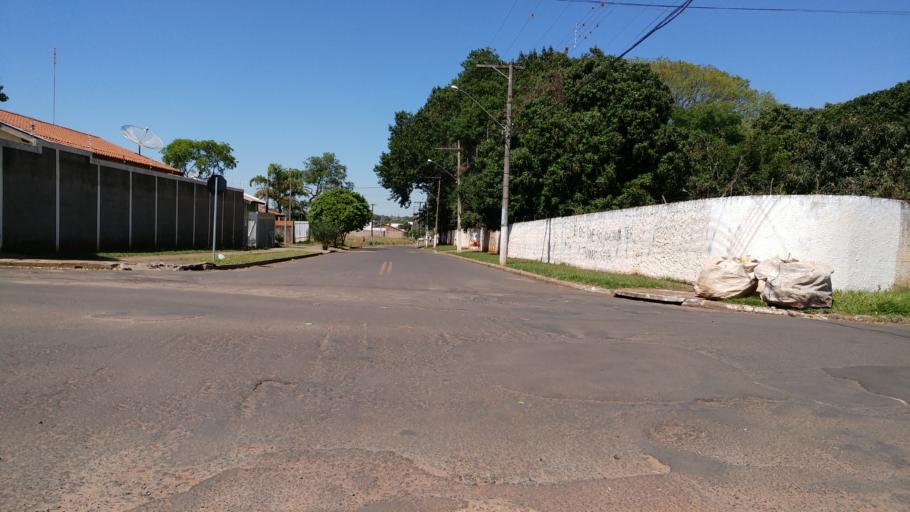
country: BR
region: Sao Paulo
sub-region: Paraguacu Paulista
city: Paraguacu Paulista
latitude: -22.4162
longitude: -50.5872
